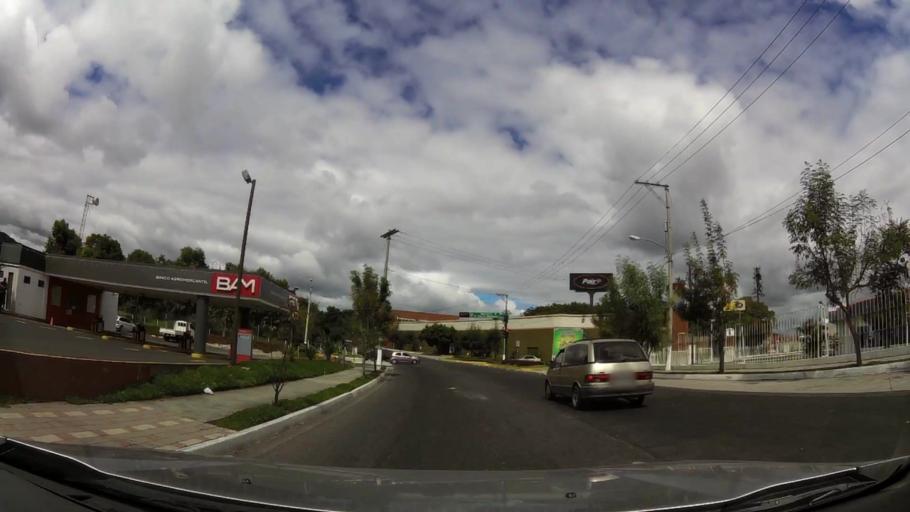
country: GT
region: Guatemala
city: Guatemala City
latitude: 14.6532
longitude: -90.5399
